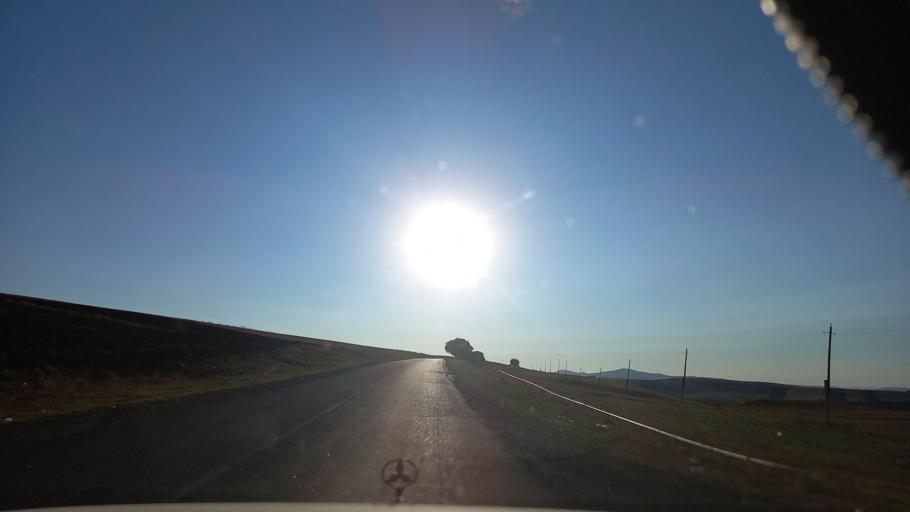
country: AZ
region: Shamkir Rayon
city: Shamkhor
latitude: 40.7660
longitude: 45.9449
